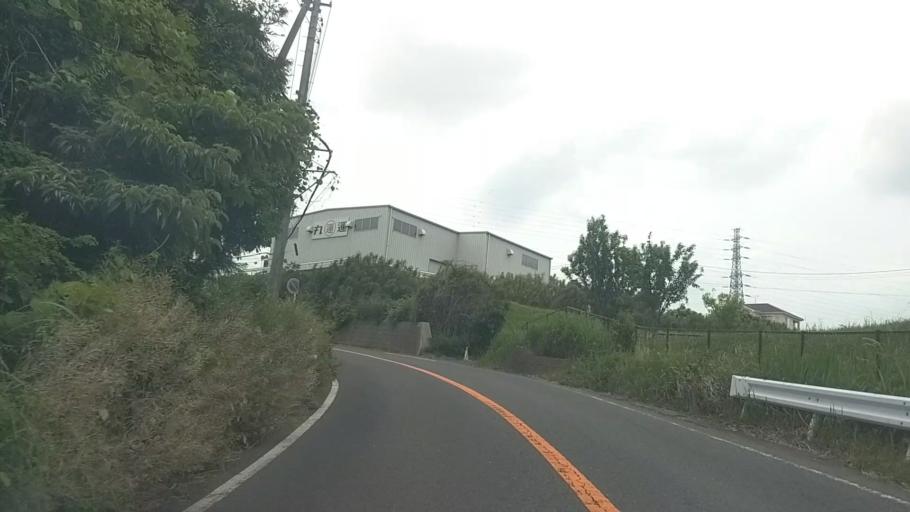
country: JP
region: Kanagawa
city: Fujisawa
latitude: 35.3601
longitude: 139.4355
